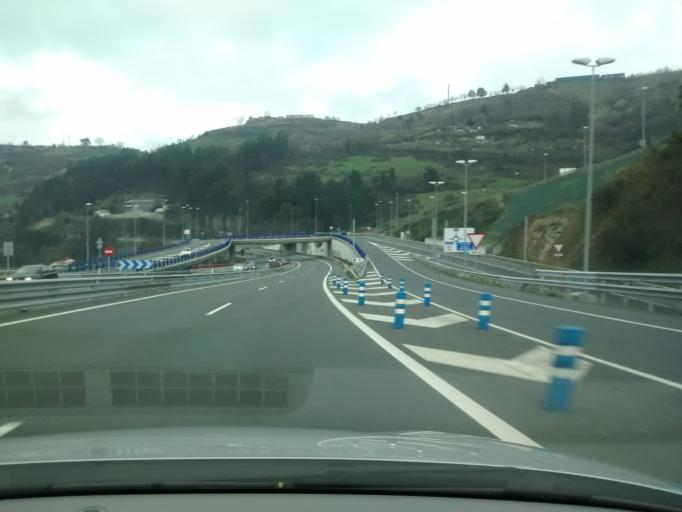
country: ES
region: Basque Country
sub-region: Bizkaia
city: Alonsotegi
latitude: 43.2542
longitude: -2.9721
